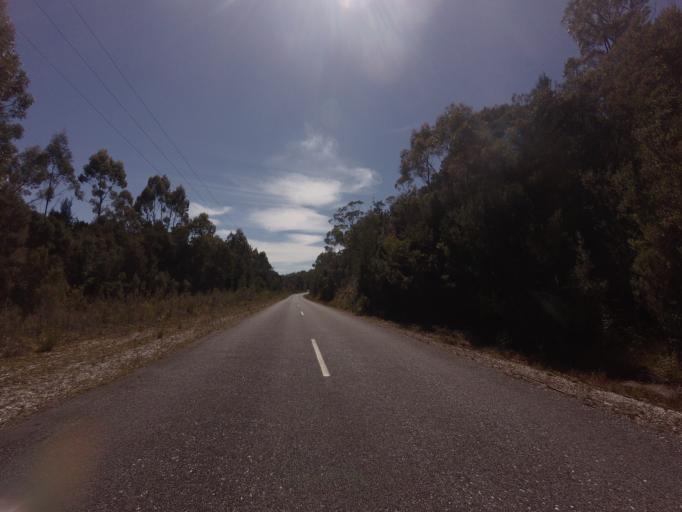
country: AU
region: Tasmania
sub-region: West Coast
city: Queenstown
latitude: -42.7793
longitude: 146.0296
